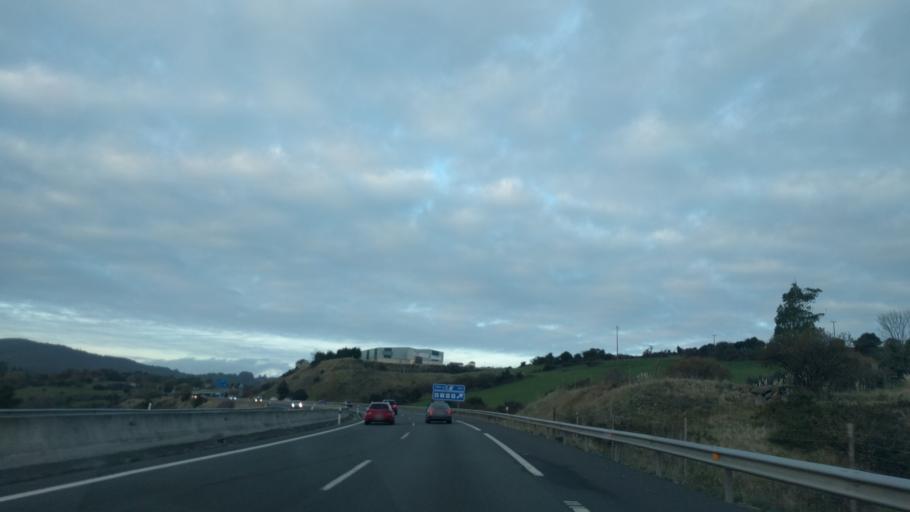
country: ES
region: Cantabria
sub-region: Provincia de Cantabria
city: Castro-Urdiales
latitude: 43.3540
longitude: -3.2158
